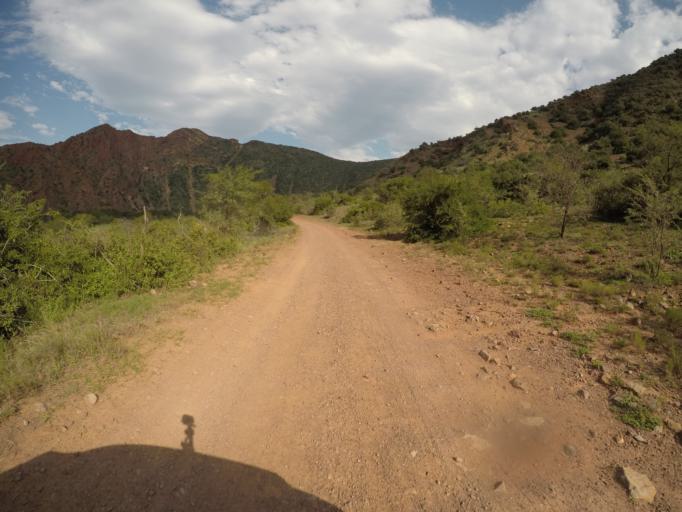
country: ZA
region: Eastern Cape
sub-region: Cacadu District Municipality
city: Kareedouw
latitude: -33.6381
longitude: 24.3164
